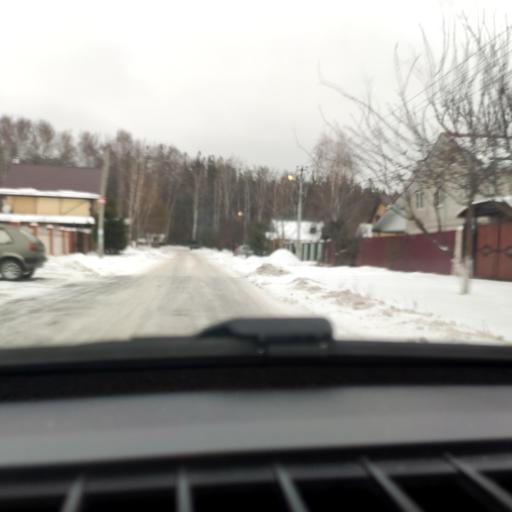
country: RU
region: Voronezj
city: Somovo
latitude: 51.6882
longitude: 39.3096
